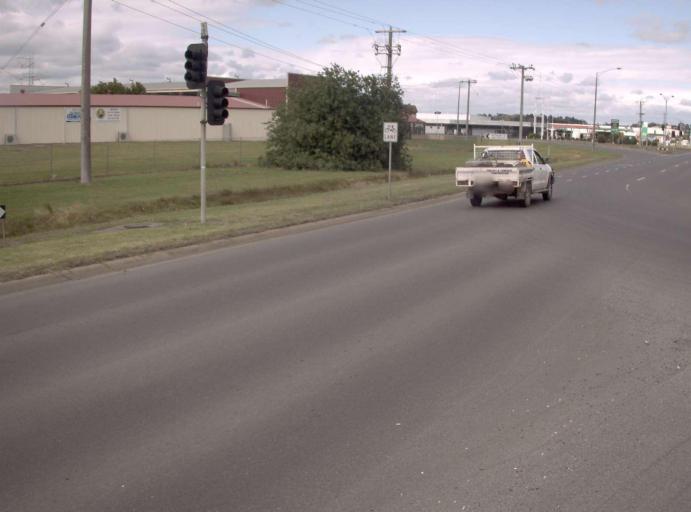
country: AU
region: Victoria
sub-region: Latrobe
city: Morwell
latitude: -38.2329
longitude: 146.4403
